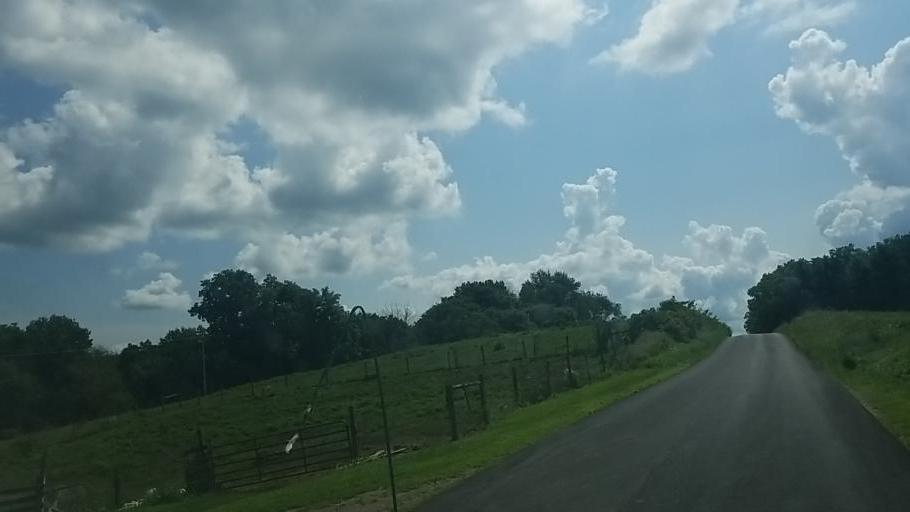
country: US
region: Ohio
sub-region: Richland County
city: Lincoln Heights
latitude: 40.6872
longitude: -82.3853
